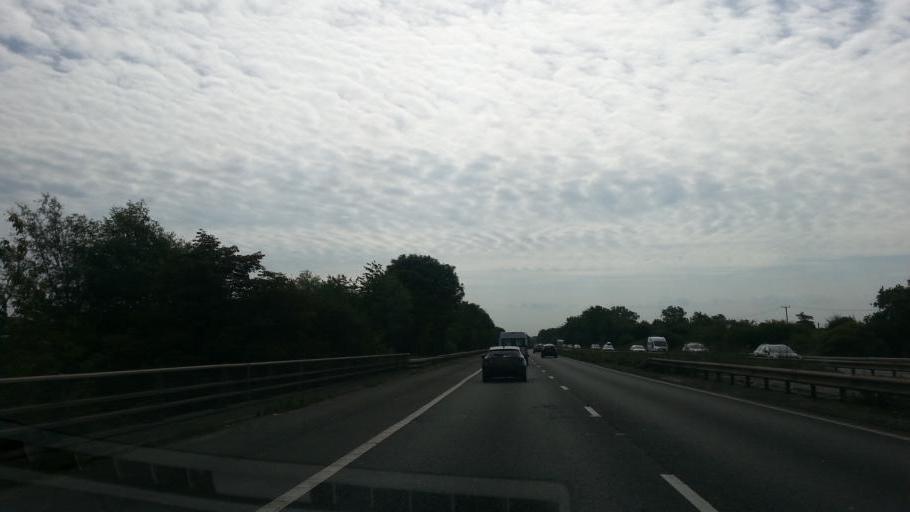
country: GB
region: England
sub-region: Hertfordshire
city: Stevenage
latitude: 51.8999
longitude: -0.2188
